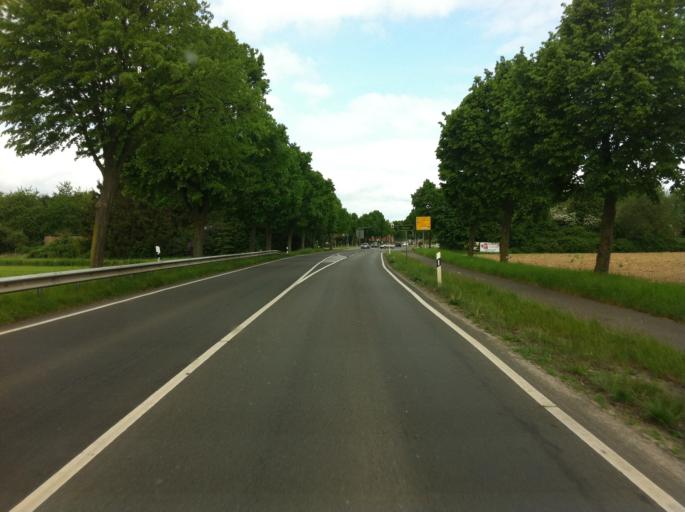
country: DE
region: North Rhine-Westphalia
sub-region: Regierungsbezirk Dusseldorf
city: Bruggen
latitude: 51.2226
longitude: 6.2030
